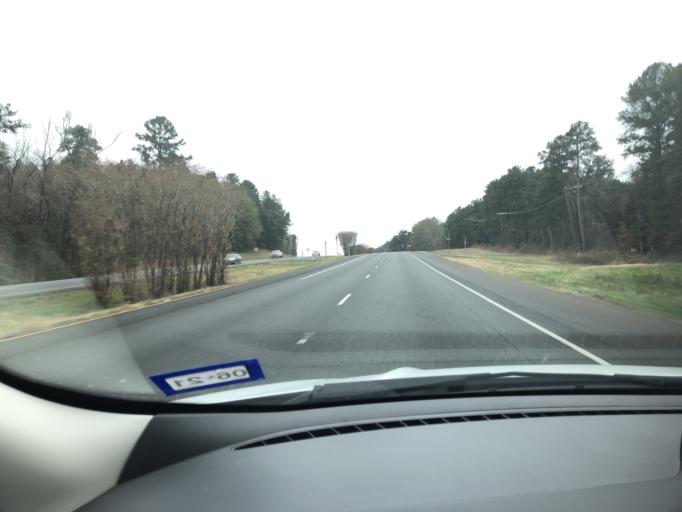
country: US
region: Texas
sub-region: Nacogdoches County
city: Nacogdoches
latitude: 31.5395
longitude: -94.6923
